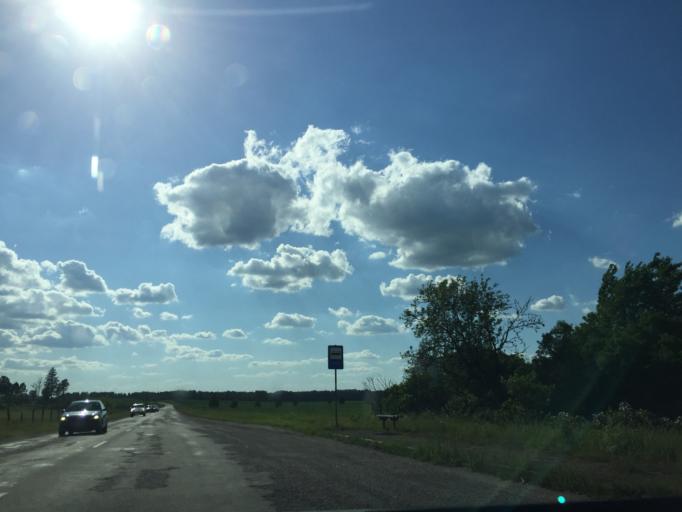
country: LV
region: Jaunpils
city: Jaunpils
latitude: 56.9088
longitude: 22.9349
